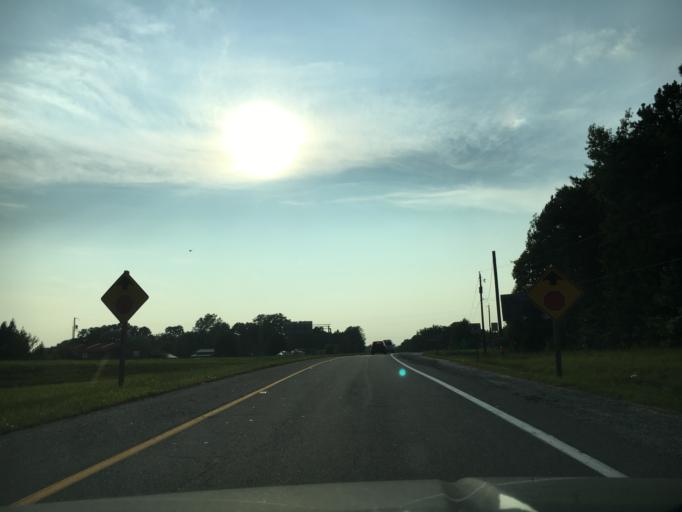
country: US
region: Virginia
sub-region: Prince Edward County
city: Farmville
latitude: 37.2733
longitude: -78.2851
